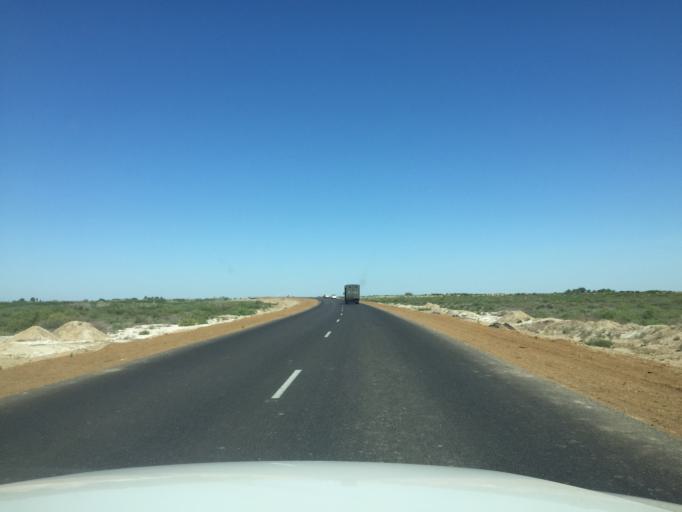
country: KZ
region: Qyzylorda
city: Dzhalagash
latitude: 44.8802
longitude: 64.7921
